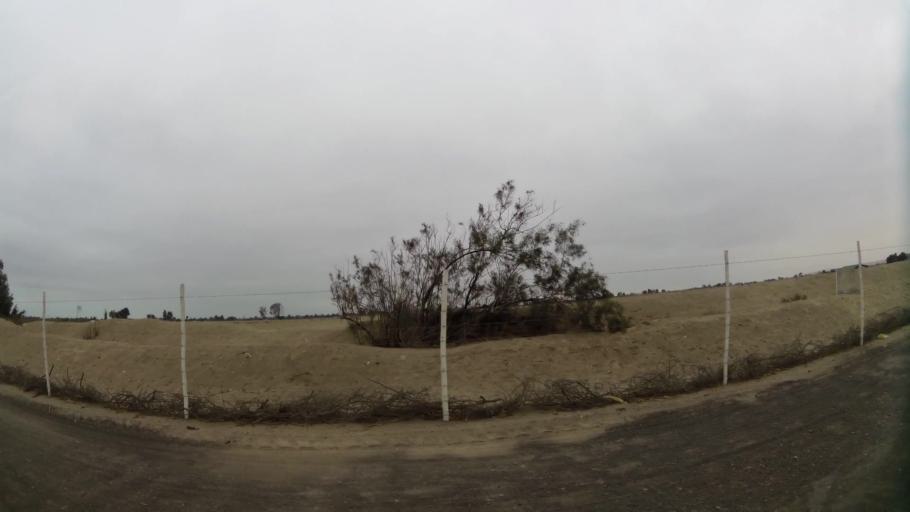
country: PE
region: Ica
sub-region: Provincia de Pisco
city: Pisco
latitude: -13.7555
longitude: -76.1817
